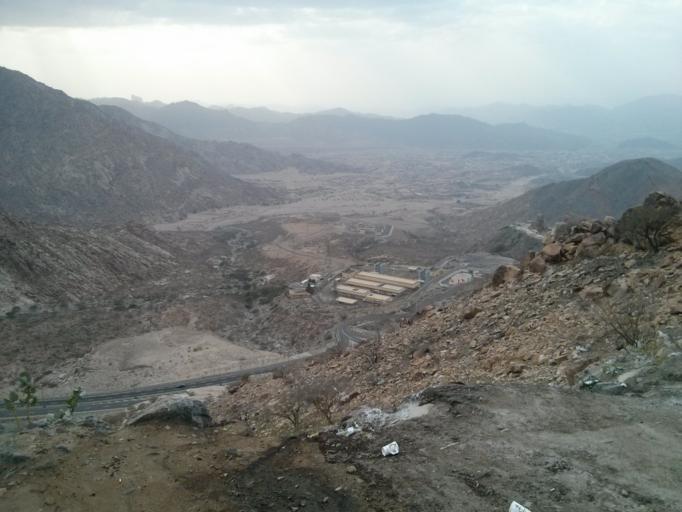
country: SA
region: Makkah
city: Al Hada
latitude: 21.3444
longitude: 40.2559
